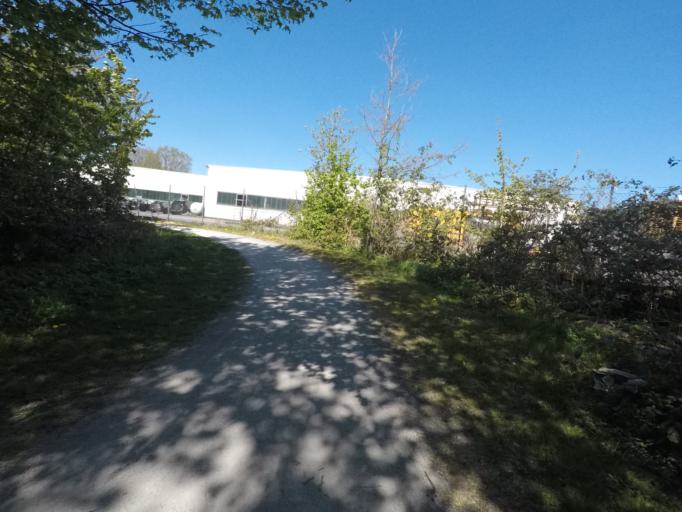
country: DE
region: North Rhine-Westphalia
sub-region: Regierungsbezirk Detmold
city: Bielefeld
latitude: 52.0369
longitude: 8.5953
